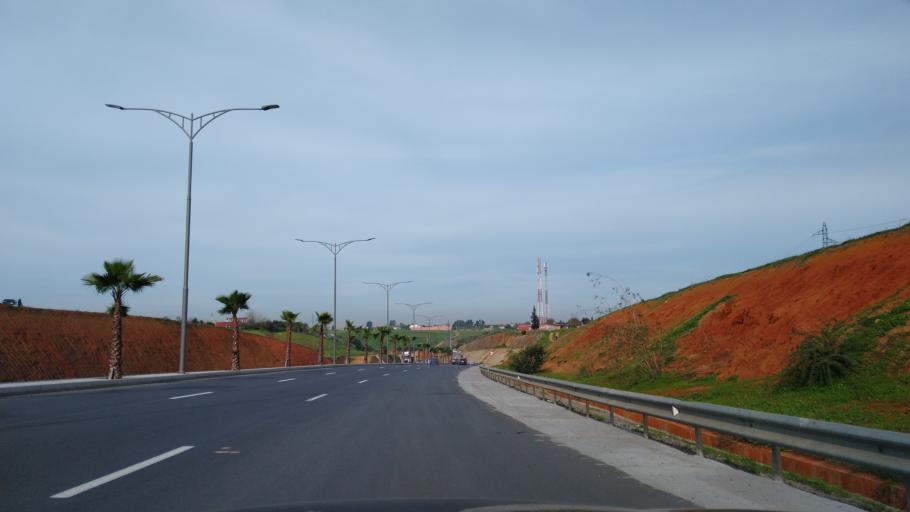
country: MA
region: Rabat-Sale-Zemmour-Zaer
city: Sale
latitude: 33.9822
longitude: -6.7425
